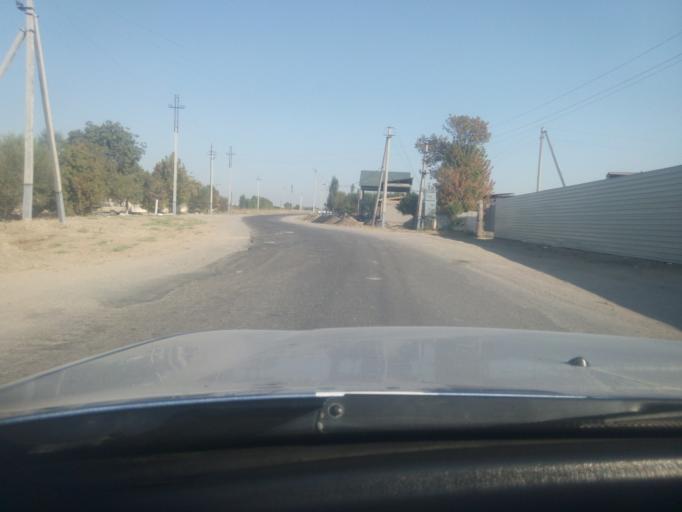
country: UZ
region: Sirdaryo
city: Guliston
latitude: 40.4956
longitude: 68.8003
